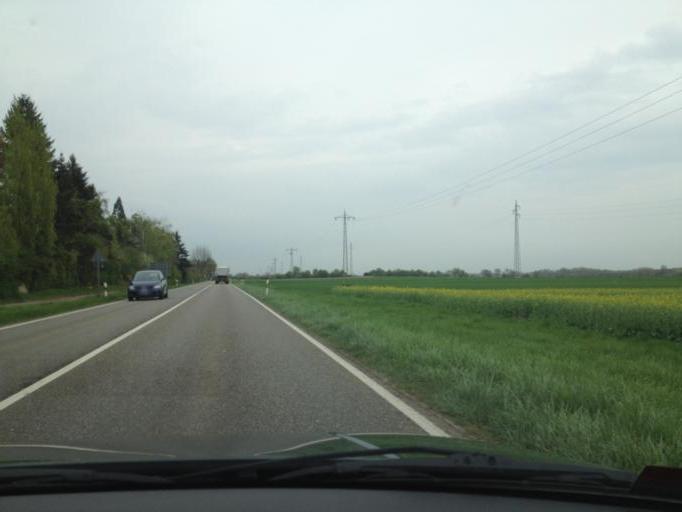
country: DE
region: Rheinland-Pfalz
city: Hochstadt
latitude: 49.2359
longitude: 8.2056
